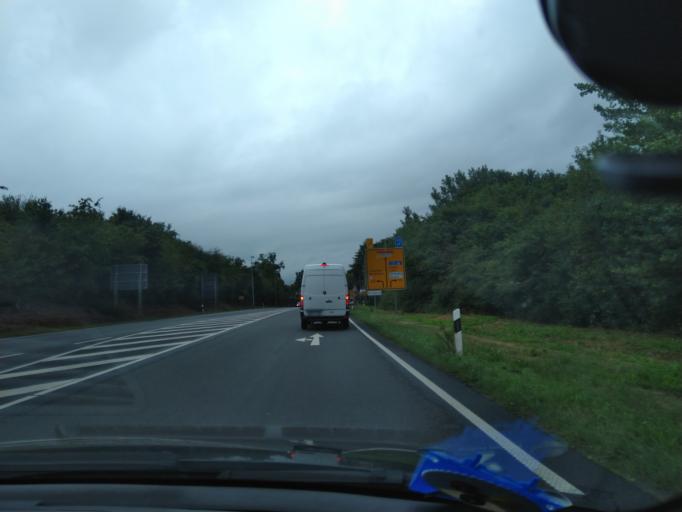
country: DE
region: Lower Saxony
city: Nordhorn
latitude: 52.4386
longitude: 7.0840
